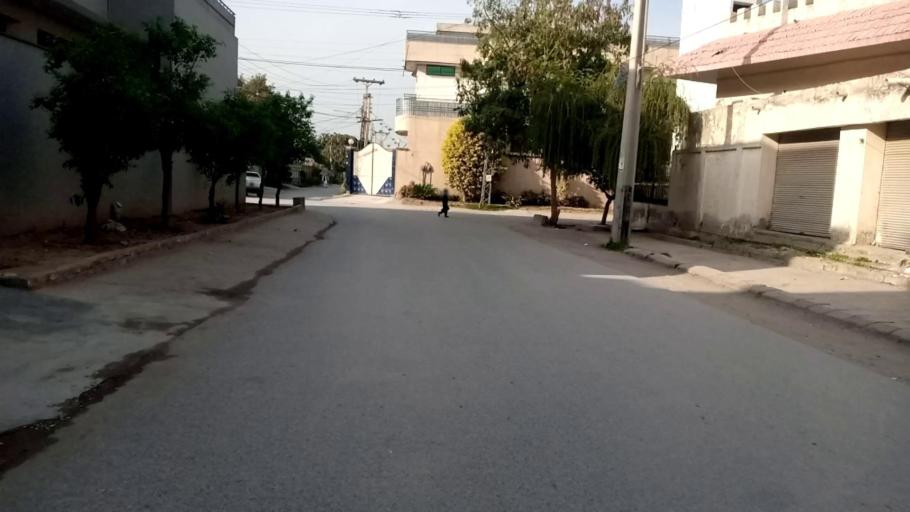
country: PK
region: Khyber Pakhtunkhwa
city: Peshawar
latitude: 33.9792
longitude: 71.4385
